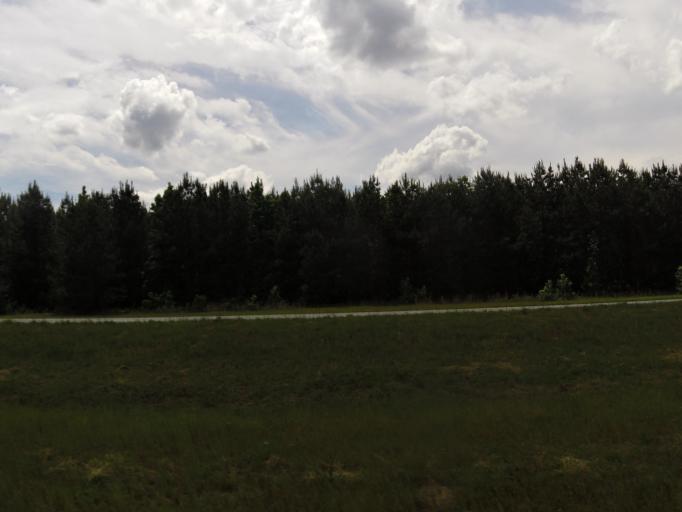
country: US
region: Georgia
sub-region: Jefferson County
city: Wadley
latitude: 32.7721
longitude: -82.3829
